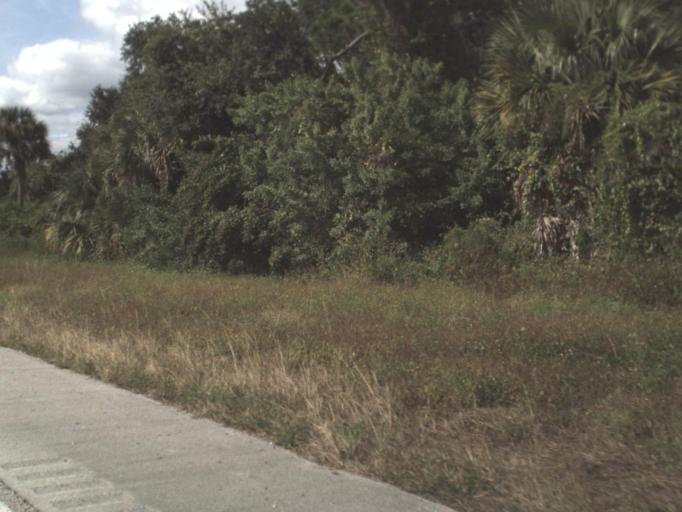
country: US
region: Florida
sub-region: Brevard County
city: Sharpes
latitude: 28.4126
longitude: -80.8351
